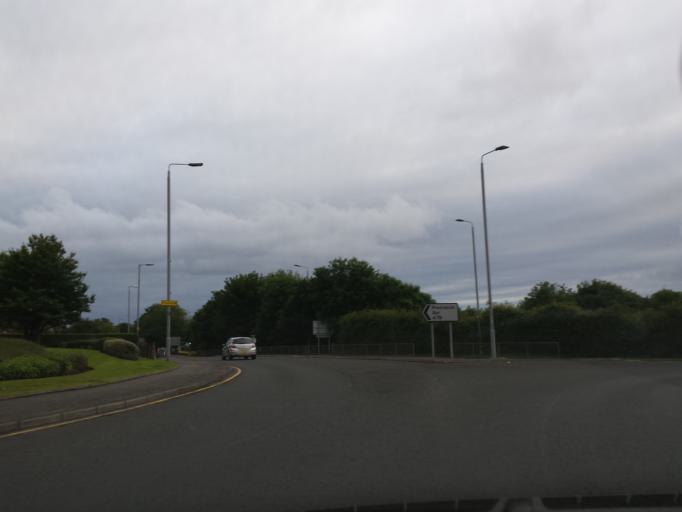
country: GB
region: Scotland
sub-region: South Ayrshire
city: Prestwick
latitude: 55.5054
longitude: -4.6064
